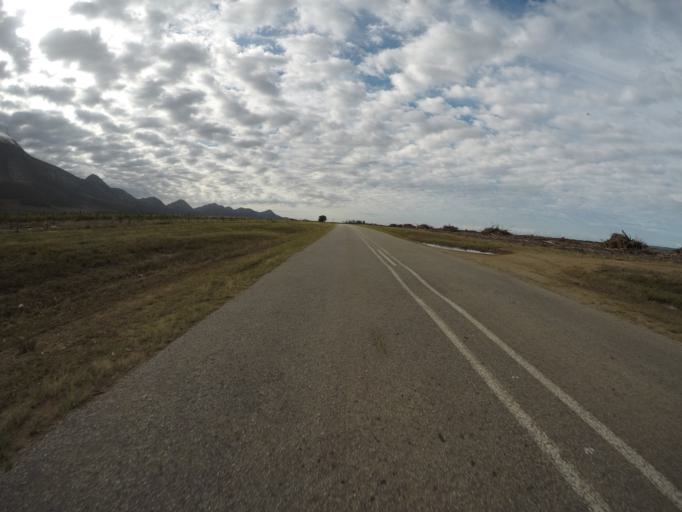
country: ZA
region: Eastern Cape
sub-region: Cacadu District Municipality
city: Kareedouw
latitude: -34.0415
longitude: 24.4106
